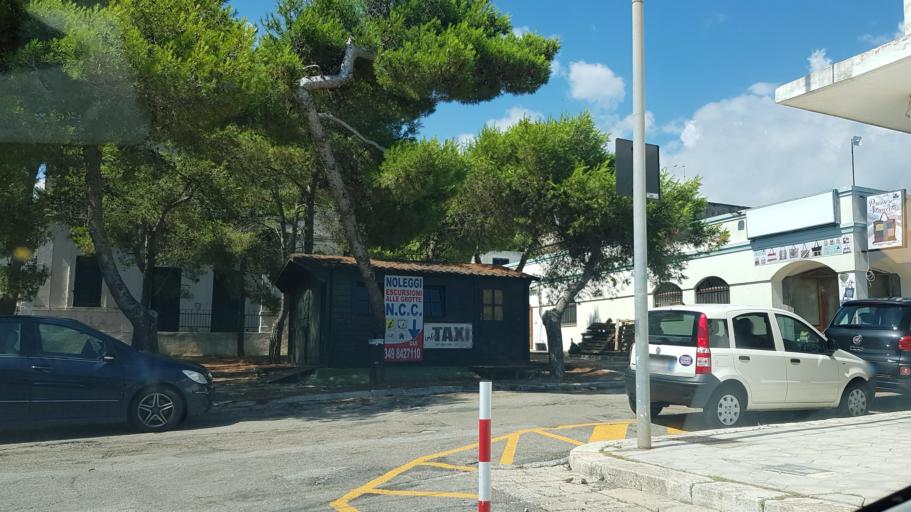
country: IT
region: Apulia
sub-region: Provincia di Lecce
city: Leuca
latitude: 39.7979
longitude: 18.3555
